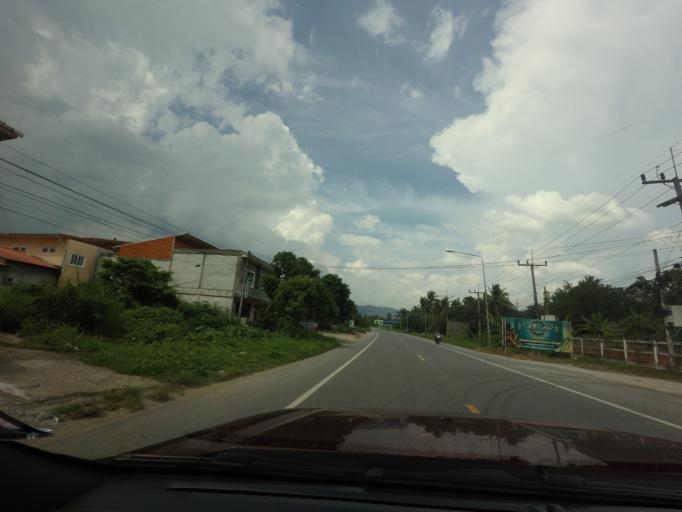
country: TH
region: Yala
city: Ban Nang Sata
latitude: 6.2575
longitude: 101.2494
